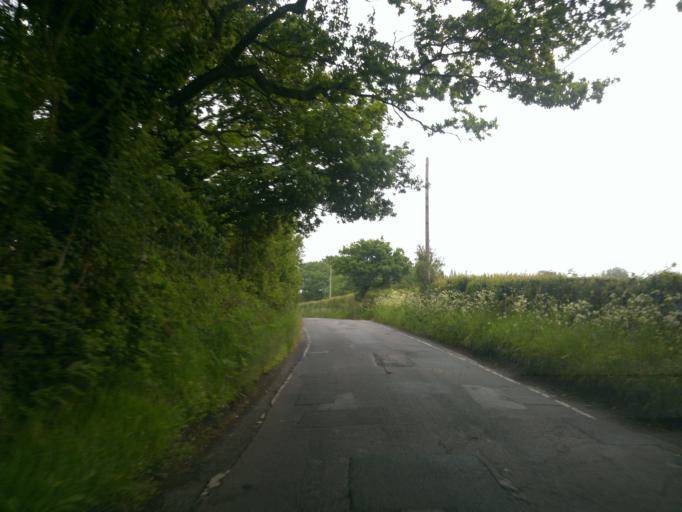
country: GB
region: England
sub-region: Essex
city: West Bergholt
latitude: 51.9042
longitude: 0.8695
